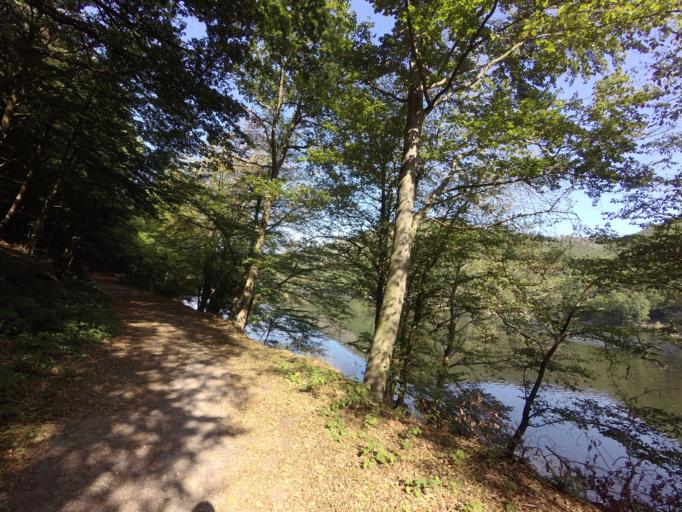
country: DE
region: North Rhine-Westphalia
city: Heimbach
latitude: 50.6050
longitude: 6.4072
